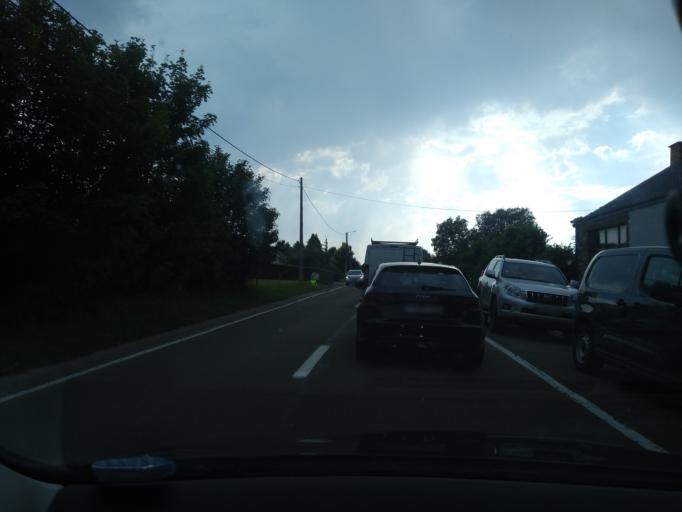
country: BE
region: Wallonia
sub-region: Province du Luxembourg
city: Sainte-Ode
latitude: 50.0264
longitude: 5.5209
